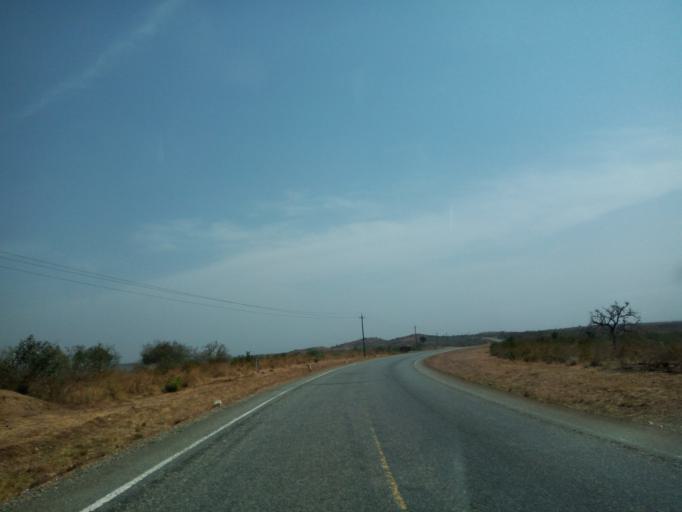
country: UG
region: Northern Region
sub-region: Nebbi District
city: Nebbi
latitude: 2.4457
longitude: 31.2545
